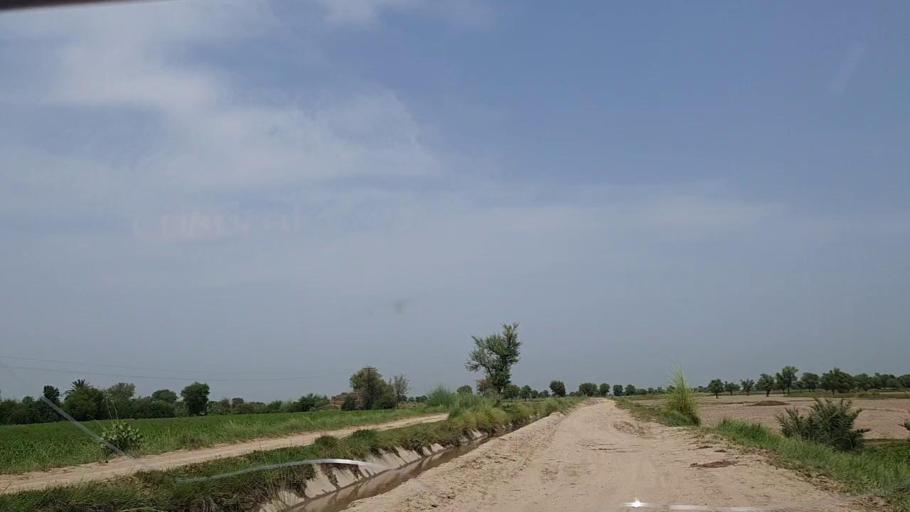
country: PK
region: Sindh
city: Tharu Shah
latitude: 26.9378
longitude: 68.0682
